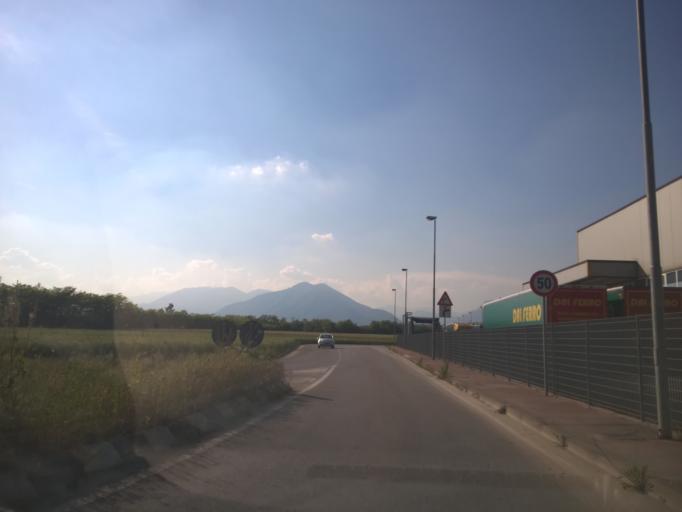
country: IT
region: Veneto
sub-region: Provincia di Vicenza
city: Sarcedo
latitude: 45.7016
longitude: 11.5091
